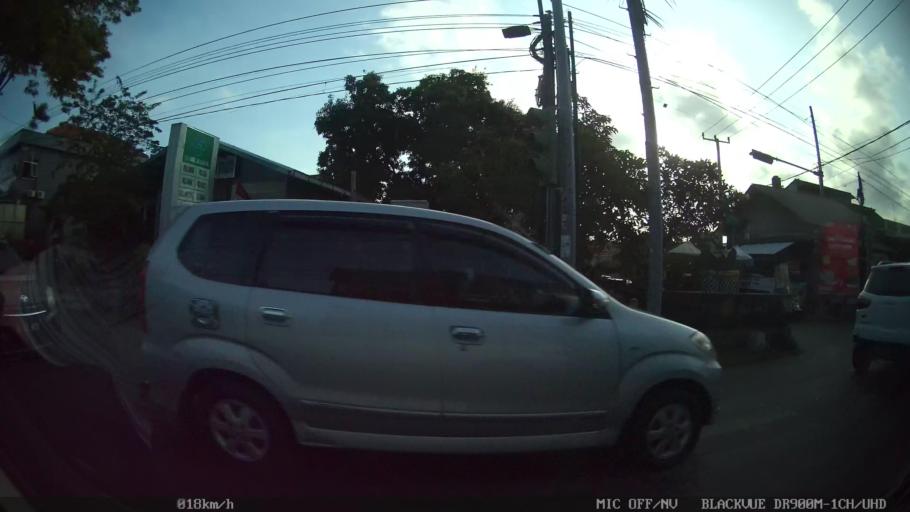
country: ID
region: Bali
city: Banjar Kertasari
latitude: -8.6288
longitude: 115.2087
